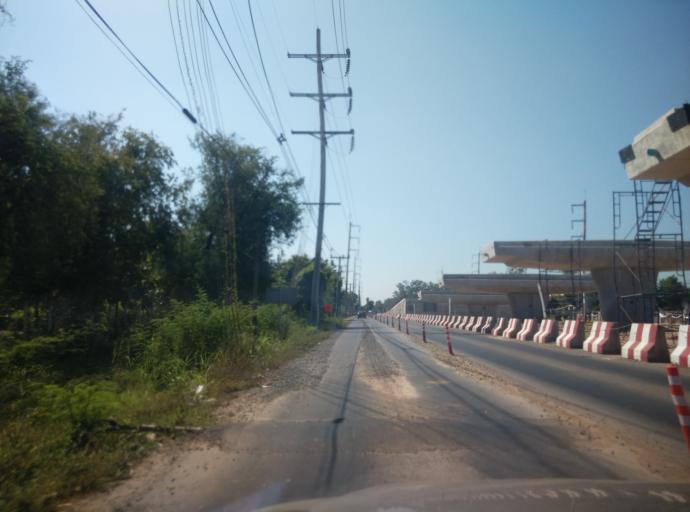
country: TH
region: Sisaket
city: Si Sa Ket
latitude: 15.1206
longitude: 104.2847
